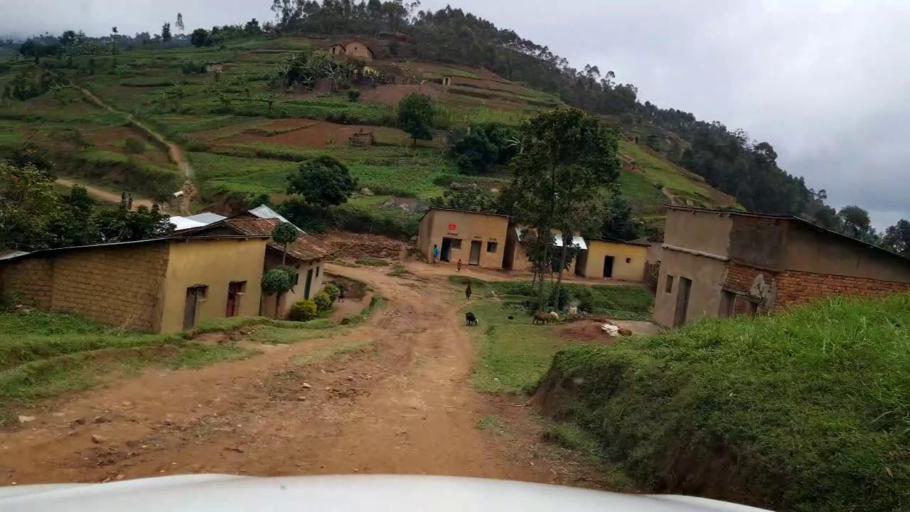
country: RW
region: Northern Province
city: Musanze
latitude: -1.5973
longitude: 29.7779
